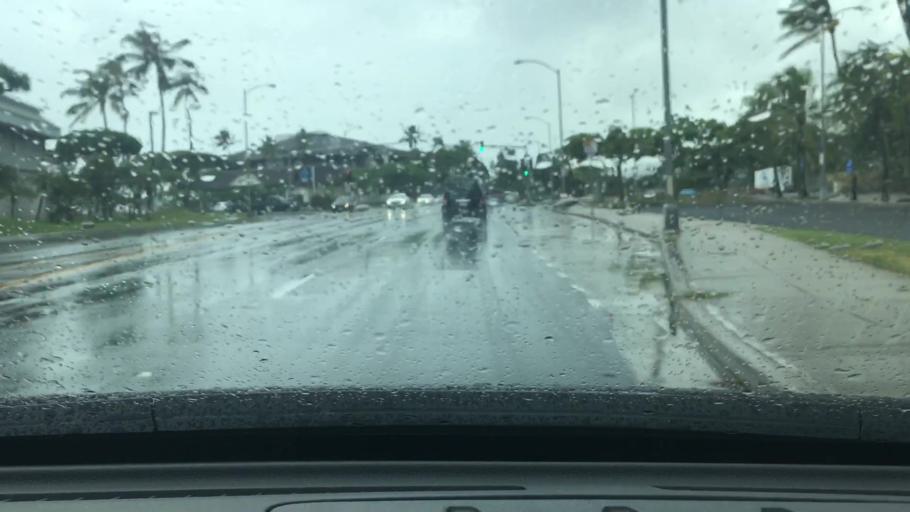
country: US
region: Hawaii
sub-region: Honolulu County
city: Waimanalo Beach
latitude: 21.2841
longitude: -157.7123
